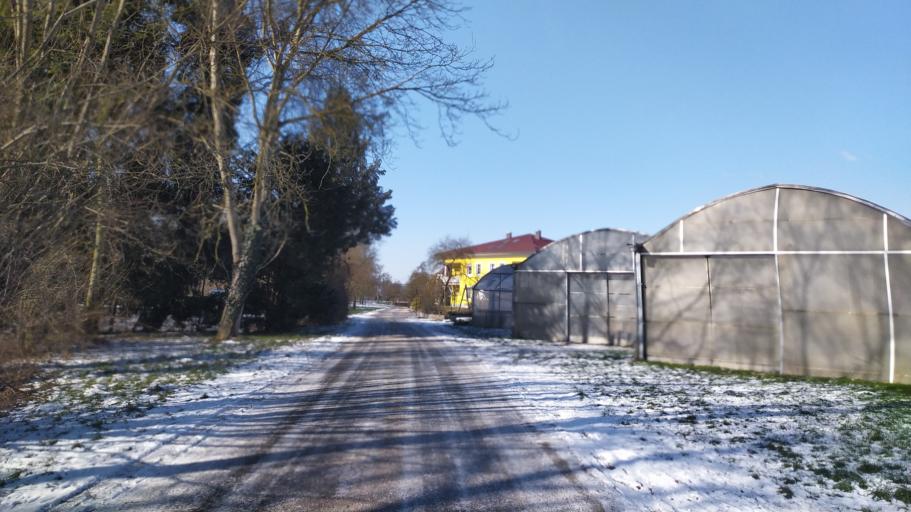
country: AT
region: Upper Austria
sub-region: Politischer Bezirk Urfahr-Umgebung
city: Goldworth
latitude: 48.3341
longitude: 14.0817
